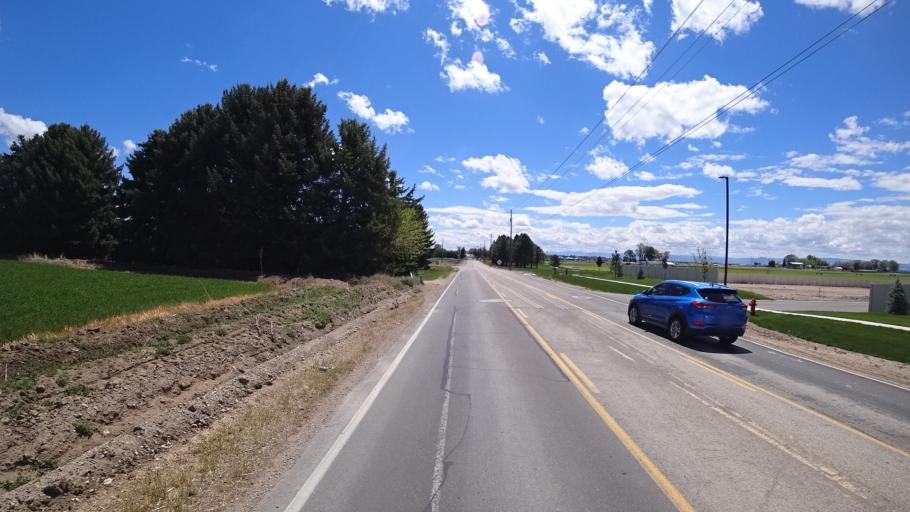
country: US
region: Idaho
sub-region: Ada County
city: Kuna
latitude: 43.5502
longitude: -116.4337
